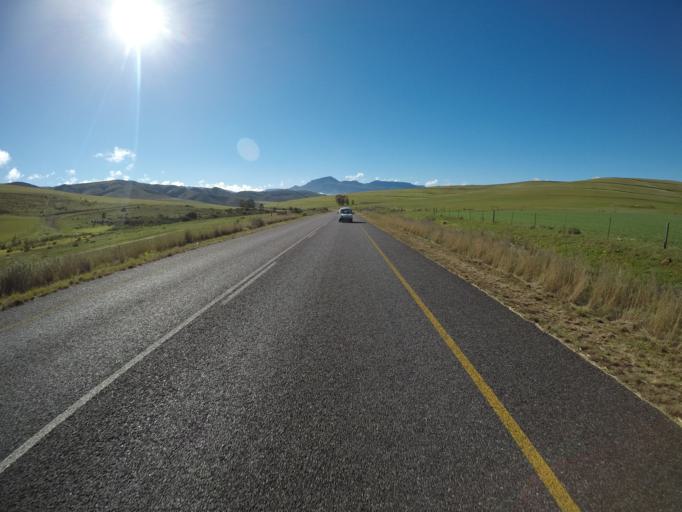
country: ZA
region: Western Cape
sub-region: Overberg District Municipality
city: Caledon
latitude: -34.1127
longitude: 19.5236
